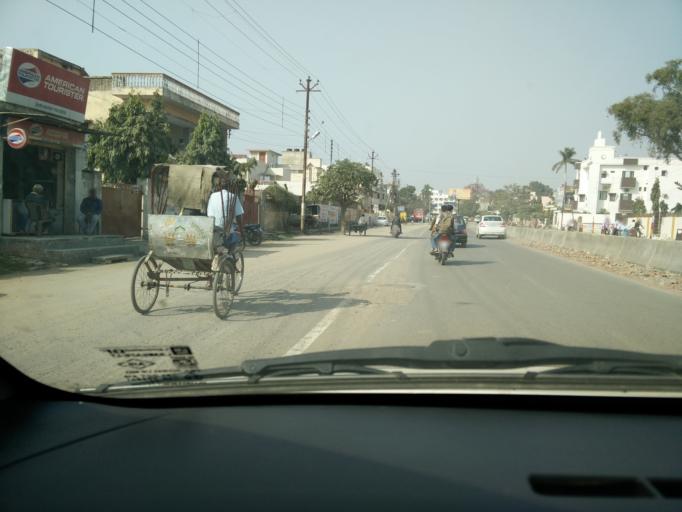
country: IN
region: Uttar Pradesh
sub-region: Varanasi
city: Varanasi
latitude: 25.2934
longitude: 83.0023
